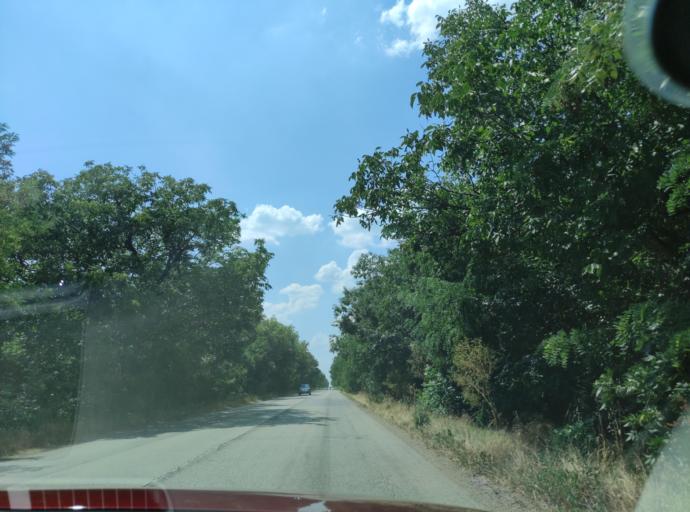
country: BG
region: Pleven
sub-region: Obshtina Dolni Dubnik
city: Dolni Dubnik
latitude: 43.4160
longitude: 24.4225
